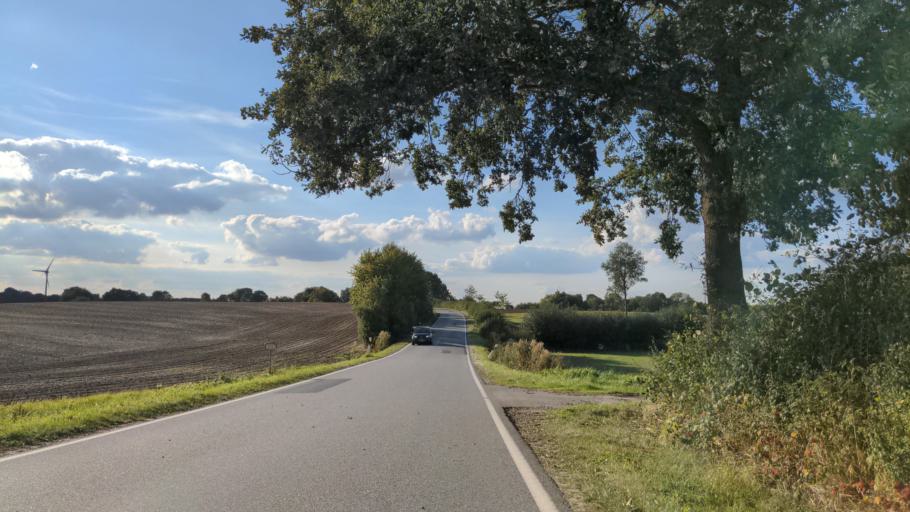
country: DE
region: Schleswig-Holstein
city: Monkhagen
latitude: 53.9461
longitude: 10.5817
